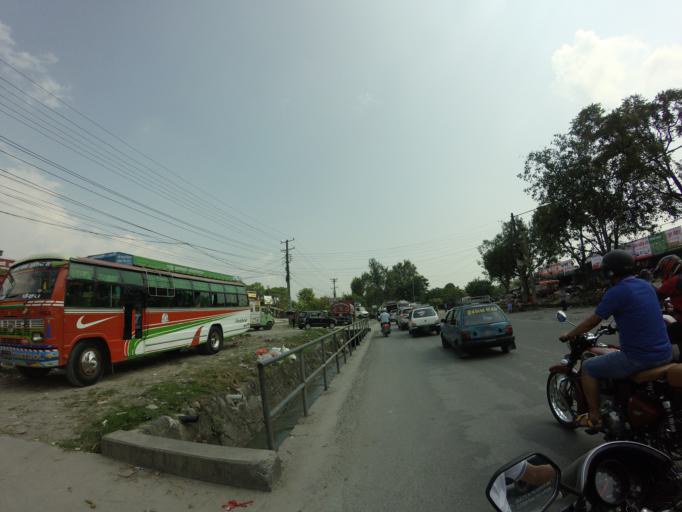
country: NP
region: Western Region
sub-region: Gandaki Zone
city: Pokhara
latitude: 28.2083
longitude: 83.9886
